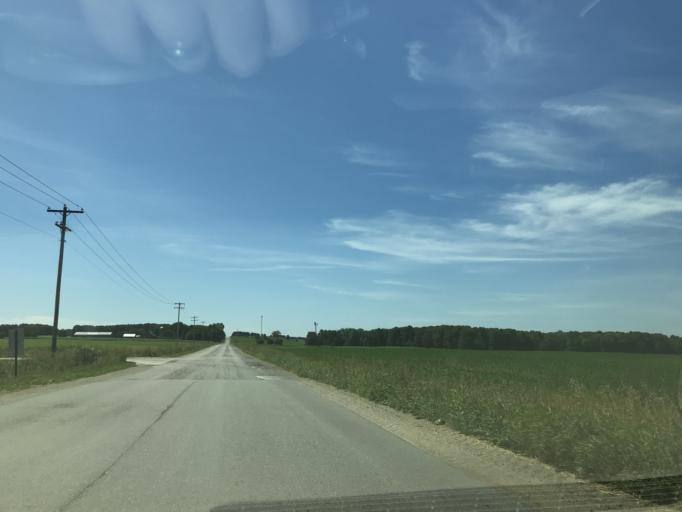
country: US
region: Michigan
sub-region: Missaukee County
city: Lake City
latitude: 44.3089
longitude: -85.0747
